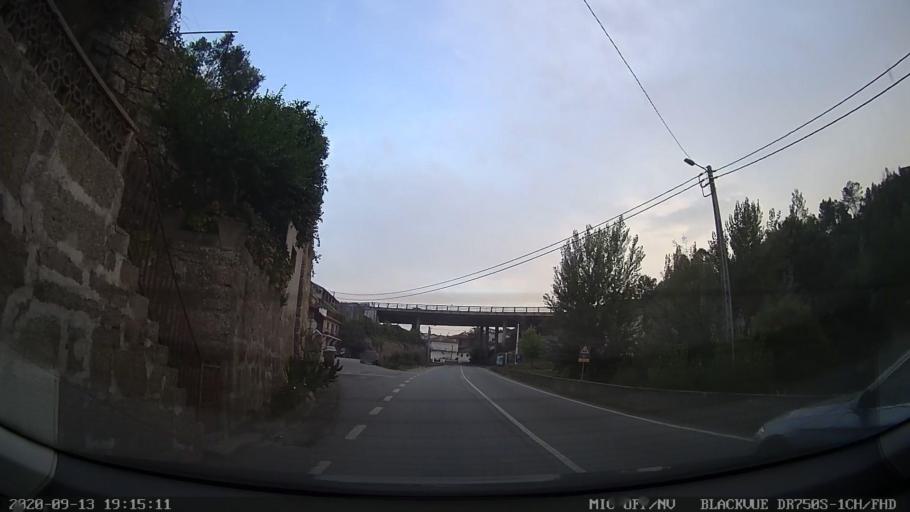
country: PT
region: Porto
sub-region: Amarante
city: Amarante
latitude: 41.2596
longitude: -8.0594
